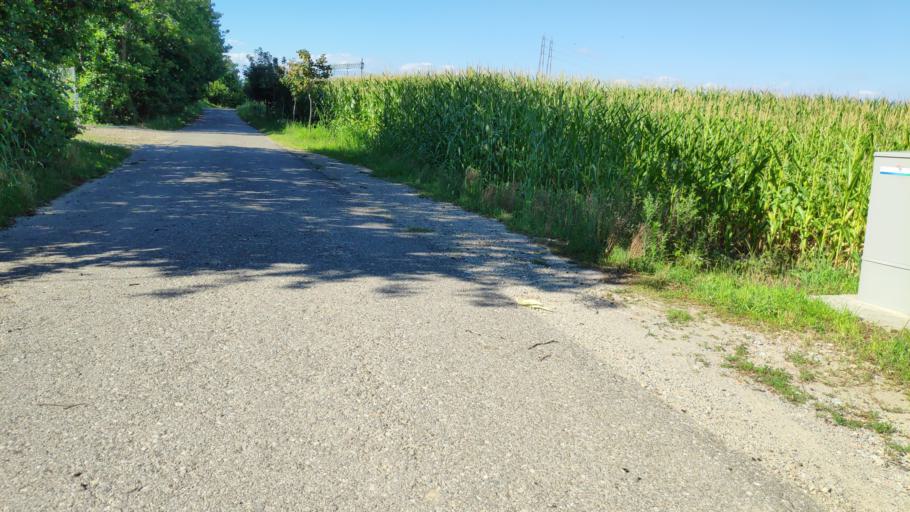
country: IT
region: Lombardy
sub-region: Citta metropolitana di Milano
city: Melzo
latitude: 45.5040
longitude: 9.4382
